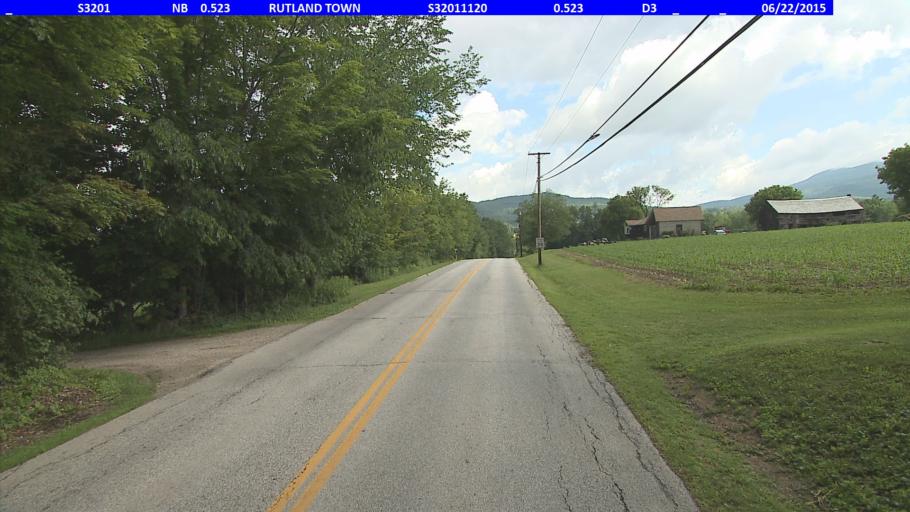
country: US
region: Vermont
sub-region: Rutland County
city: Rutland
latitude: 43.6454
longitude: -72.9740
